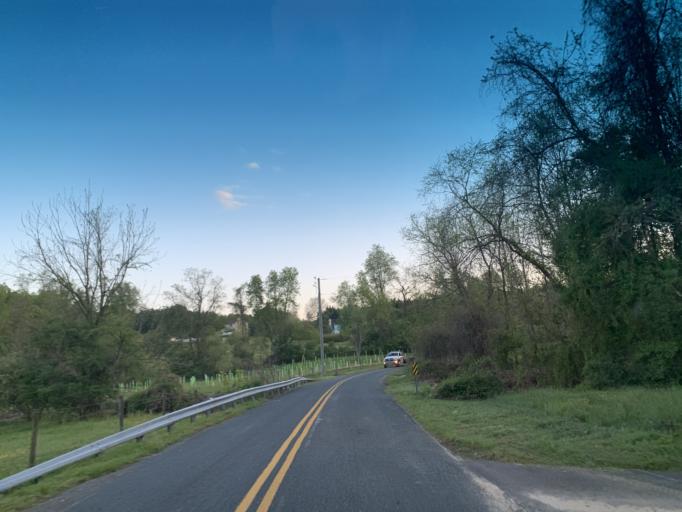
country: US
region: Maryland
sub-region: Harford County
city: Bel Air South
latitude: 39.5369
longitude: -76.2767
